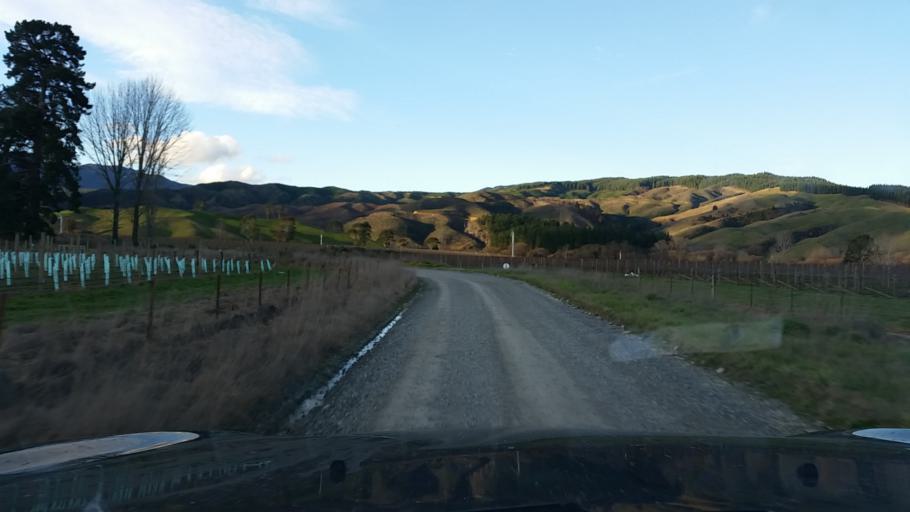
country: NZ
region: Marlborough
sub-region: Marlborough District
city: Blenheim
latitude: -41.5176
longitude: 173.5841
